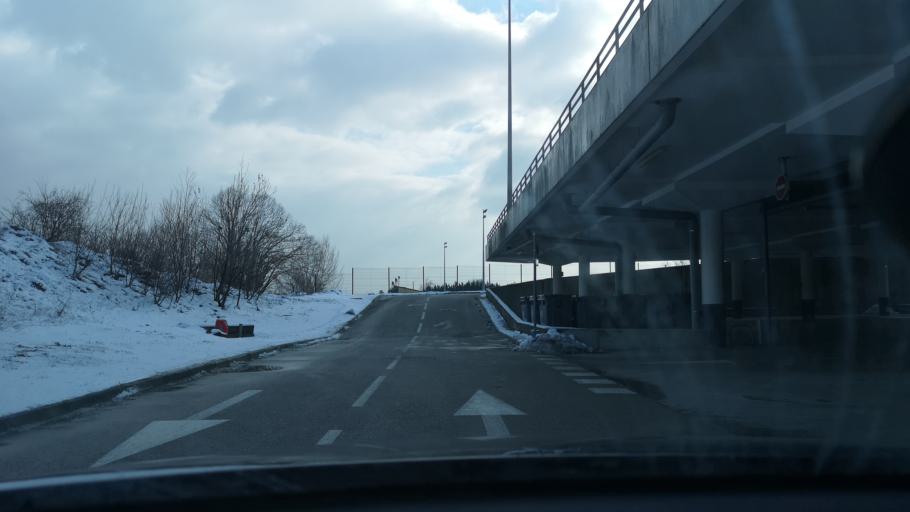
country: FR
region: Rhone-Alpes
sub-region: Departement de l'Ain
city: Lancrans
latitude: 46.1243
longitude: 5.8144
